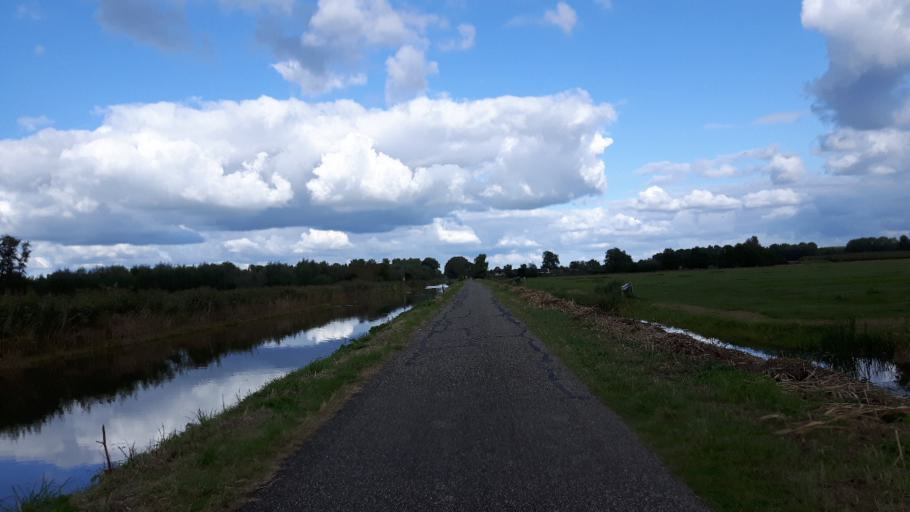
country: NL
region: South Holland
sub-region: Gemeente Leerdam
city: Leerdam
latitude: 51.9050
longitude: 5.1279
